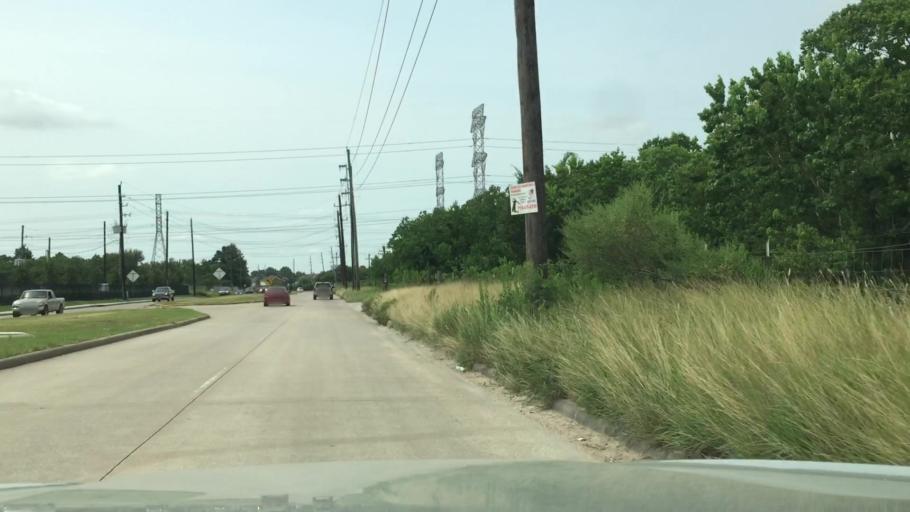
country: US
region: Texas
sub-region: Harris County
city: Jersey Village
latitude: 29.9402
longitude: -95.5469
